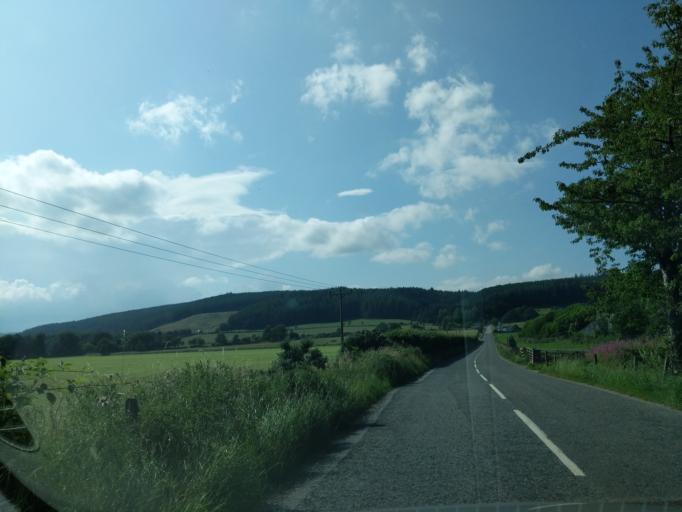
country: GB
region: Scotland
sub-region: Moray
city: Rothes
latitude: 57.5508
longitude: -3.1418
